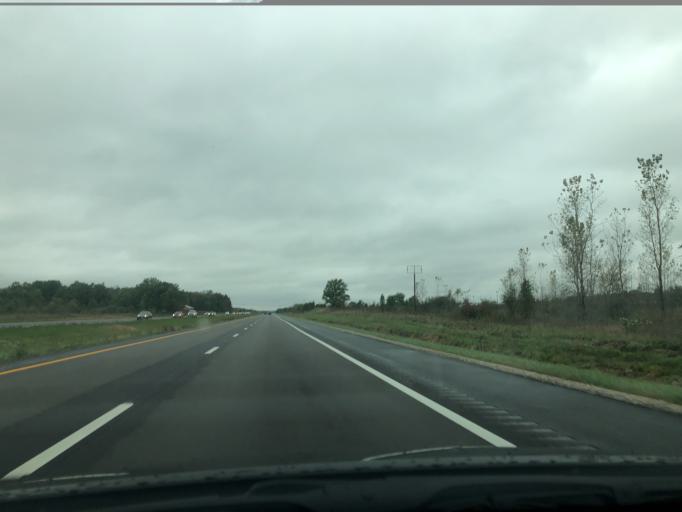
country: US
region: Ohio
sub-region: Union County
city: Marysville
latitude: 40.2579
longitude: -83.4595
